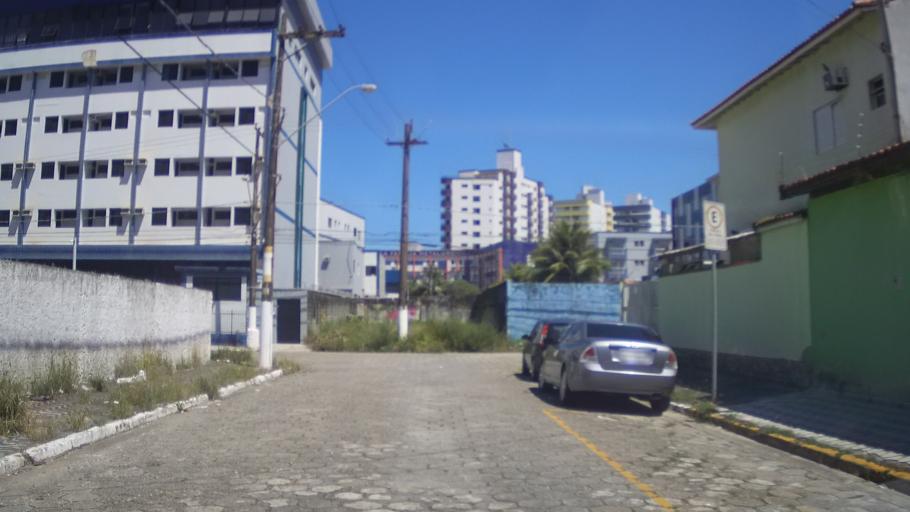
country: BR
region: Sao Paulo
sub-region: Praia Grande
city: Praia Grande
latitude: -24.0303
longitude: -46.4808
